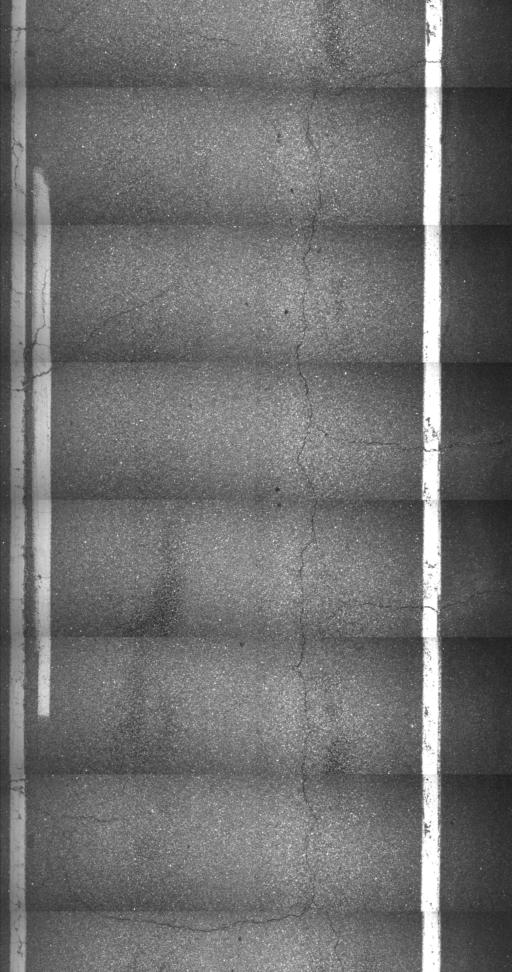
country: US
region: New Hampshire
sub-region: Sullivan County
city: Claremont
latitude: 43.3384
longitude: -72.4079
